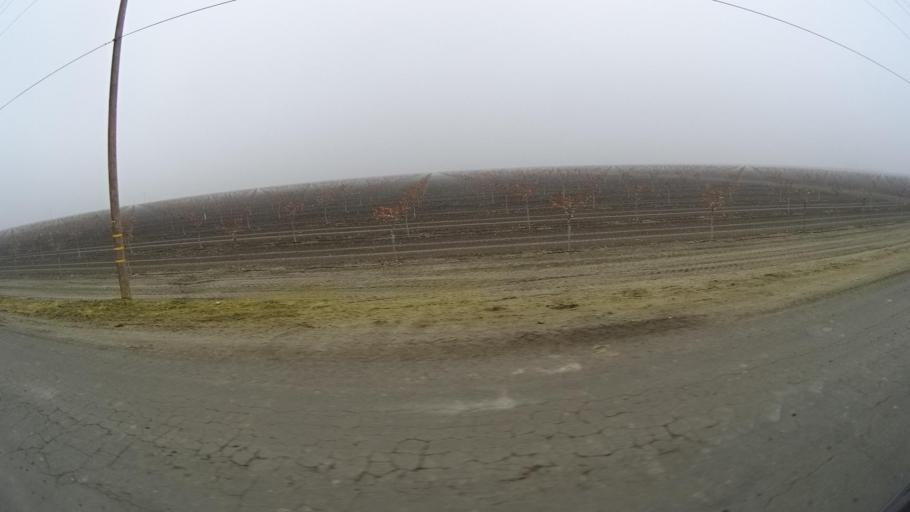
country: US
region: California
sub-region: Kern County
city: Buttonwillow
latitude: 35.4448
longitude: -119.5178
